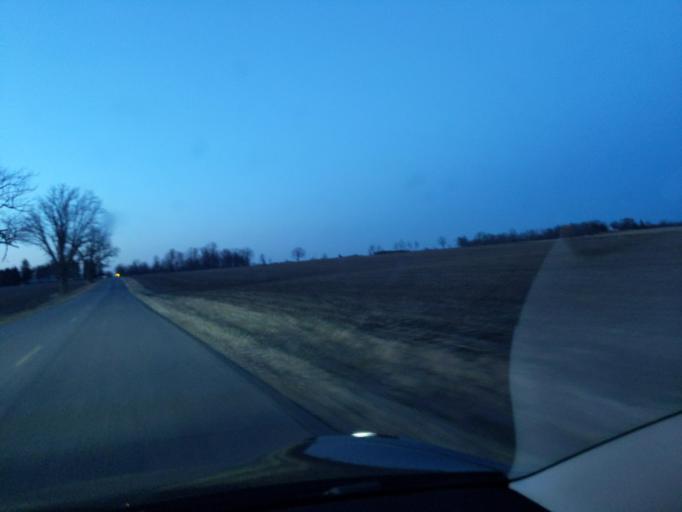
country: US
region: Michigan
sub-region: Ingham County
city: Stockbridge
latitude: 42.5284
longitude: -84.2206
